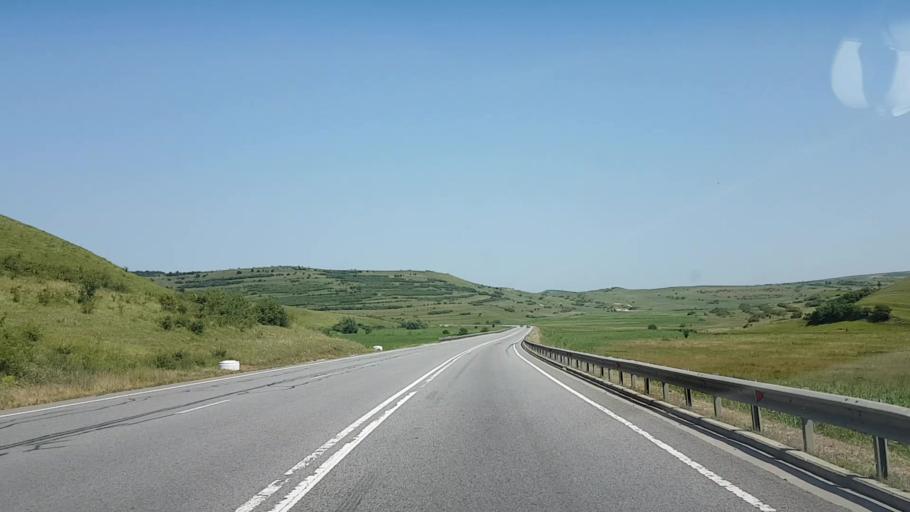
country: RO
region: Cluj
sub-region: Comuna Feleacu
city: Gheorghieni
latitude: 46.7329
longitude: 23.6945
